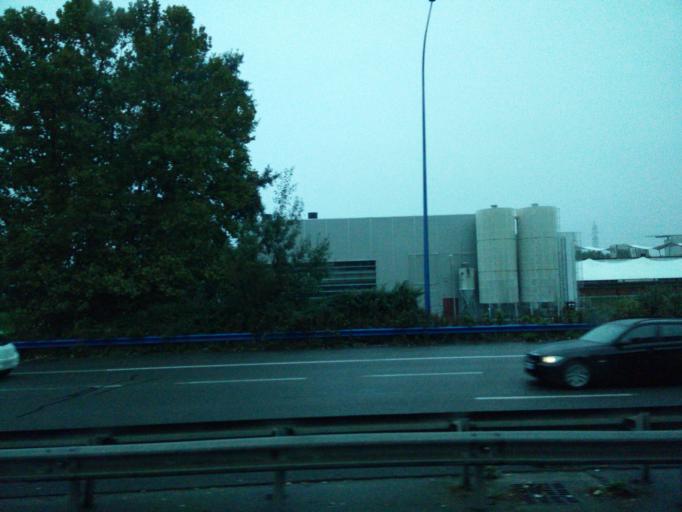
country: FR
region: Midi-Pyrenees
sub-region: Departement de la Haute-Garonne
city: Blagnac
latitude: 43.6298
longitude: 1.4203
